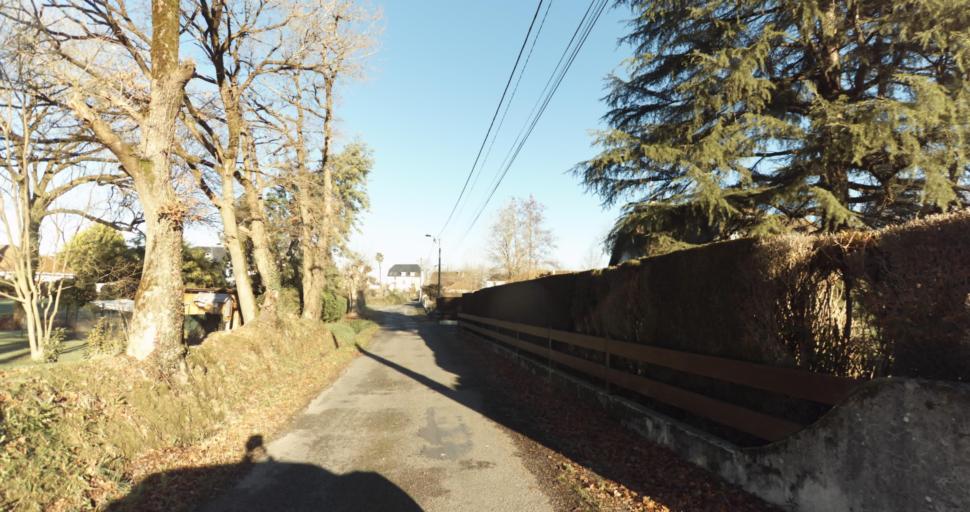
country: FR
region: Aquitaine
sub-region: Departement des Pyrenees-Atlantiques
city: Morlaas
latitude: 43.3395
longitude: -0.2630
